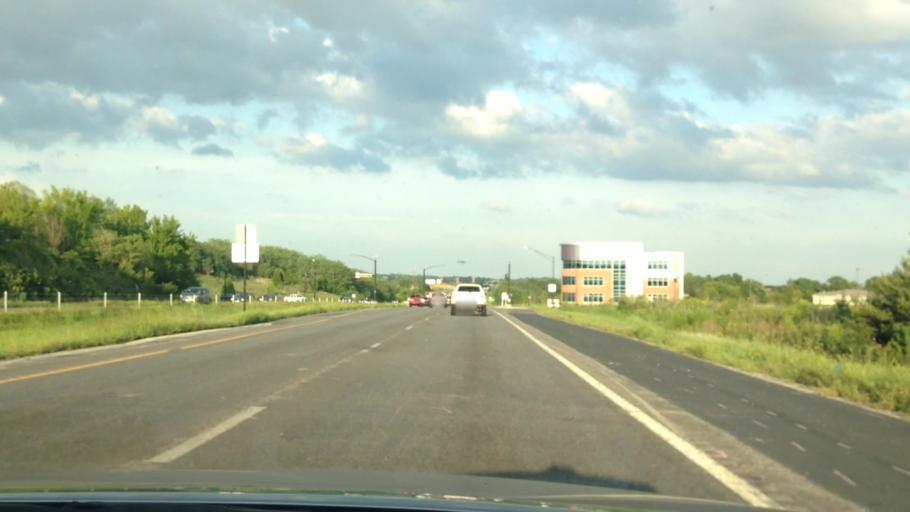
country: US
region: Missouri
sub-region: Clay County
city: Pleasant Valley
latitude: 39.2442
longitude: -94.4900
